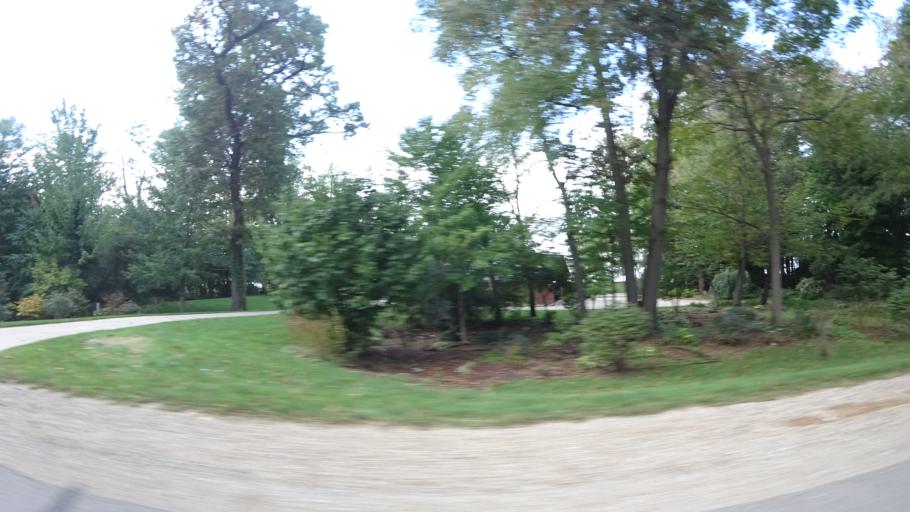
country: US
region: Michigan
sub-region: Saint Joseph County
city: Centreville
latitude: 41.9845
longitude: -85.5663
